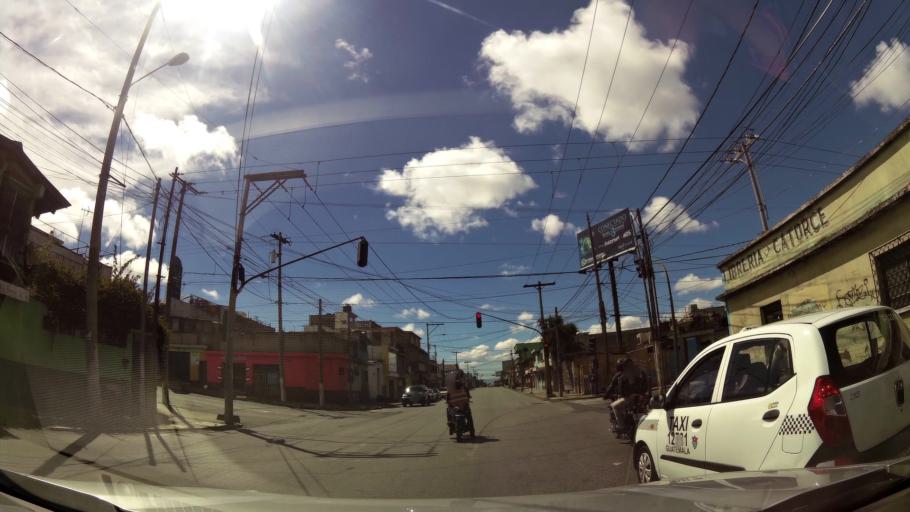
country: GT
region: Guatemala
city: Guatemala City
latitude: 14.6071
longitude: -90.5354
